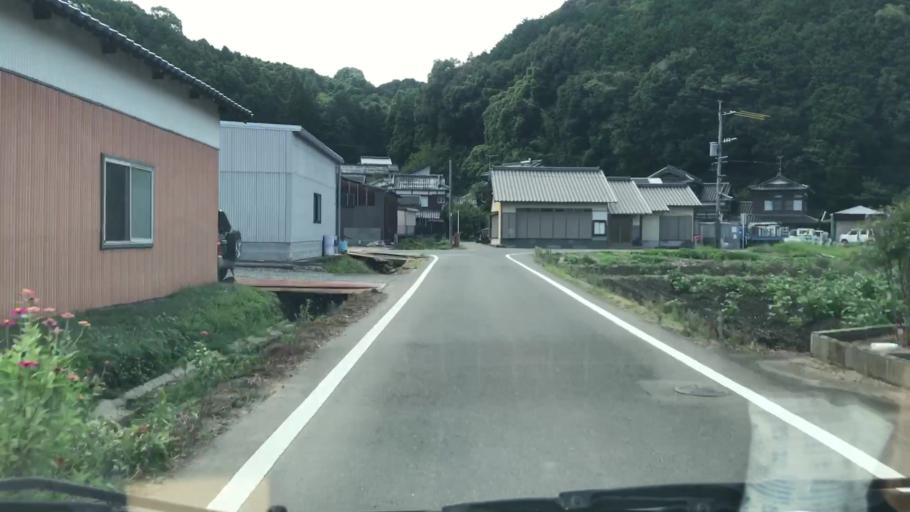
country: JP
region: Saga Prefecture
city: Kashima
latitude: 33.1176
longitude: 130.0707
